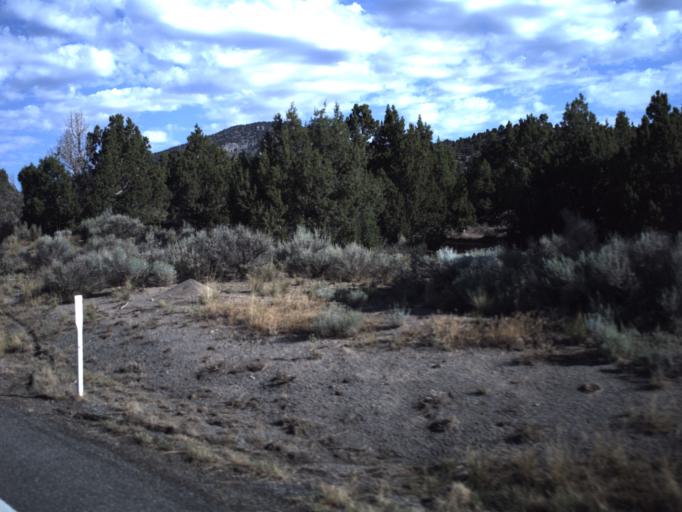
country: US
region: Utah
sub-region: Utah County
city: Genola
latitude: 39.9654
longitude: -112.0479
